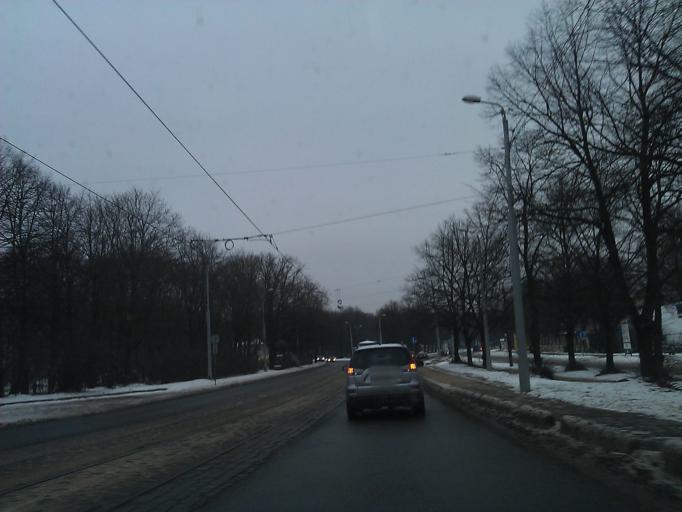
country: LV
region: Riga
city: Riga
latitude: 56.9801
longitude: 24.1476
